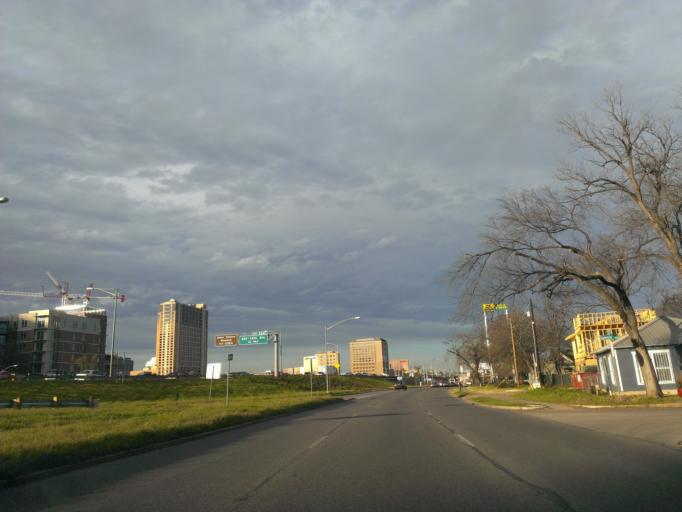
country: US
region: Texas
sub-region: Travis County
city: Austin
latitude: 30.2586
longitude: -97.7365
